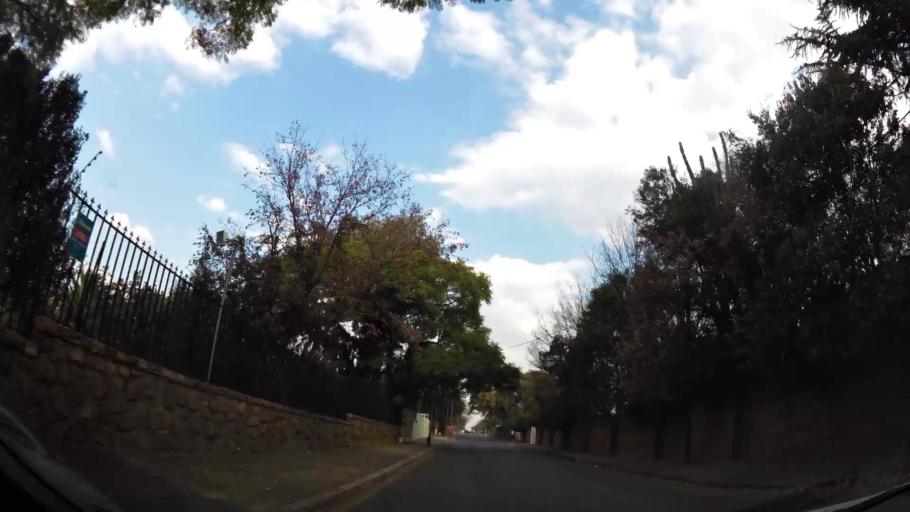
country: ZA
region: Gauteng
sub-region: Ekurhuleni Metropolitan Municipality
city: Germiston
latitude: -26.2374
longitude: 28.1685
